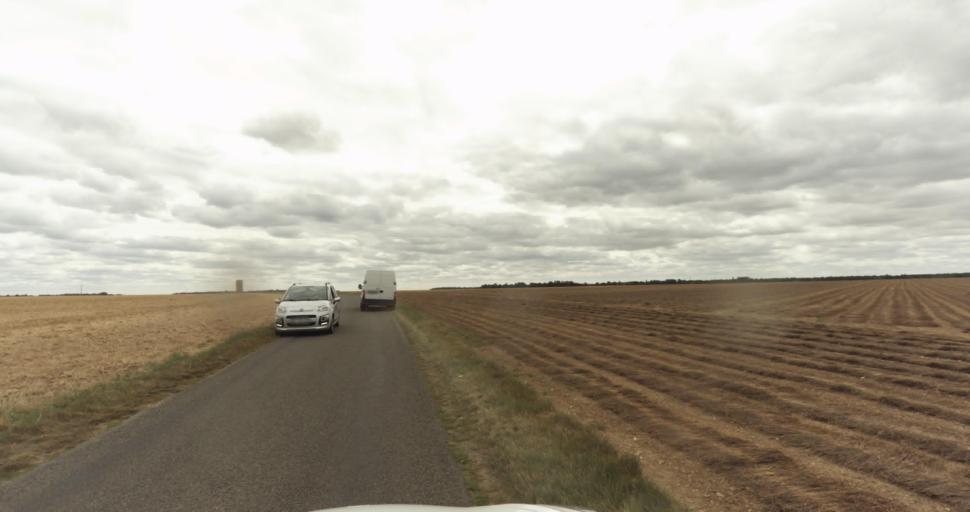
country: FR
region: Centre
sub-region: Departement d'Eure-et-Loir
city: Saint-Remy-sur-Avre
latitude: 48.8118
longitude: 1.2430
